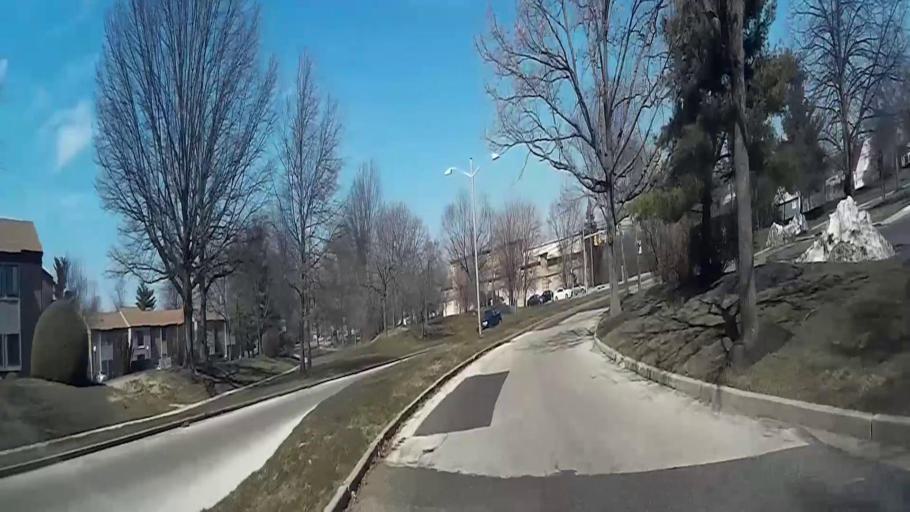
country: US
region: New Jersey
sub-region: Burlington County
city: Marlton
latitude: 39.8916
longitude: -74.9302
